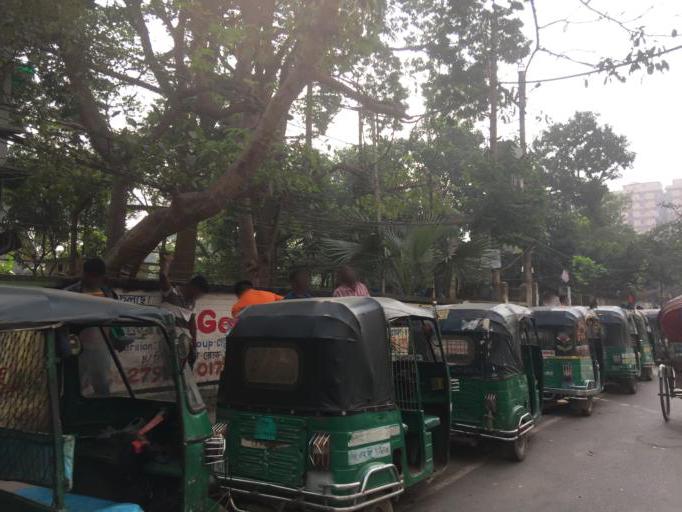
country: BD
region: Dhaka
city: Azimpur
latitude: 23.7386
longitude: 90.3742
